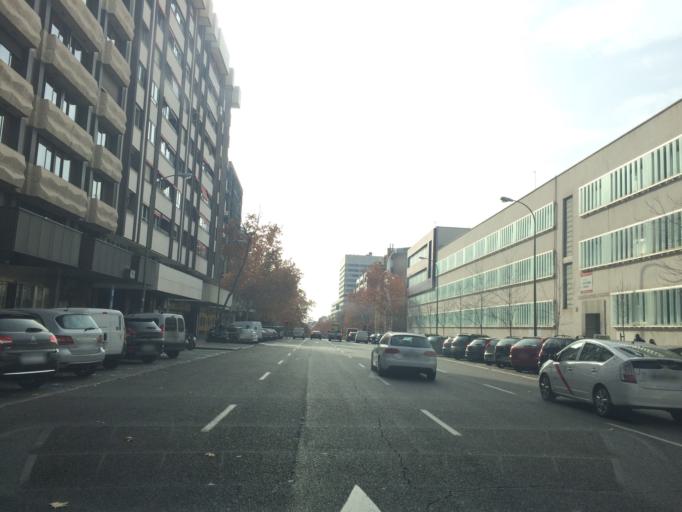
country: ES
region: Madrid
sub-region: Provincia de Madrid
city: Chamartin
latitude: 40.4621
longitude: -3.6939
